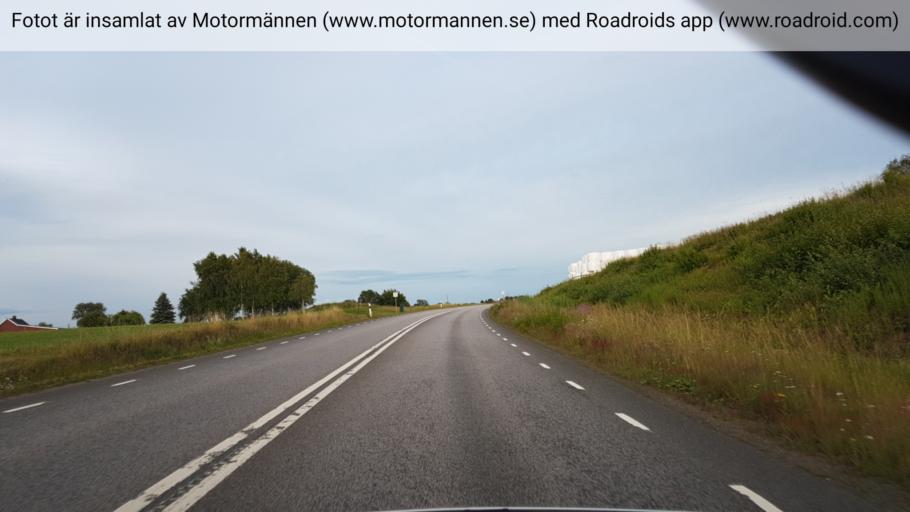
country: SE
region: Vaestra Goetaland
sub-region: Falkopings Kommun
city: Falkoeping
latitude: 58.2409
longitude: 13.5370
